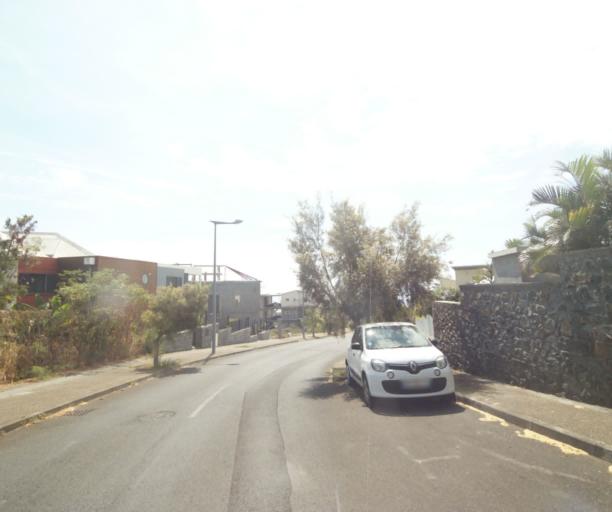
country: RE
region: Reunion
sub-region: Reunion
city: Saint-Paul
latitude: -21.0503
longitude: 55.2621
